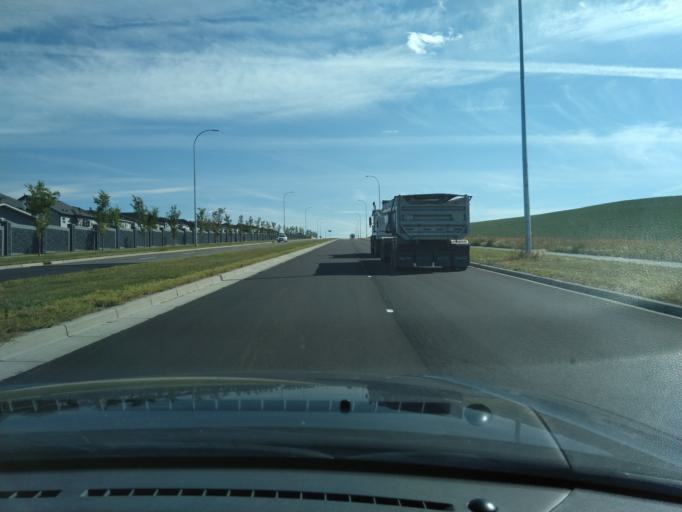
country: CA
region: Alberta
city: Calgary
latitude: 51.1794
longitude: -114.1762
